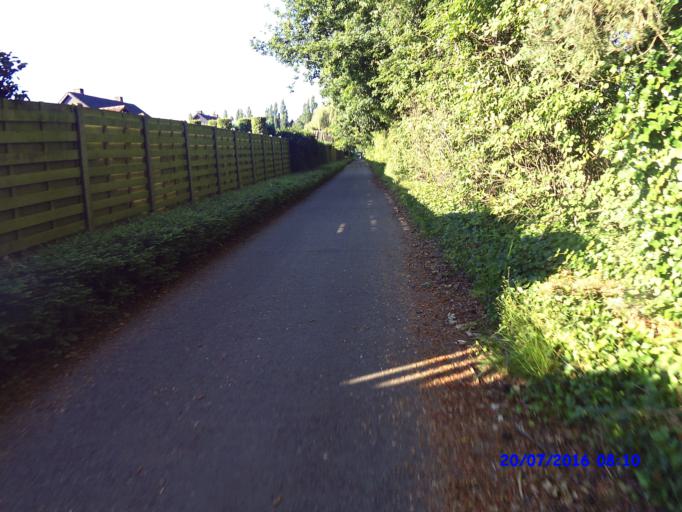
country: BE
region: Flanders
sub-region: Provincie Antwerpen
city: Turnhout
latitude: 51.3069
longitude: 4.9301
